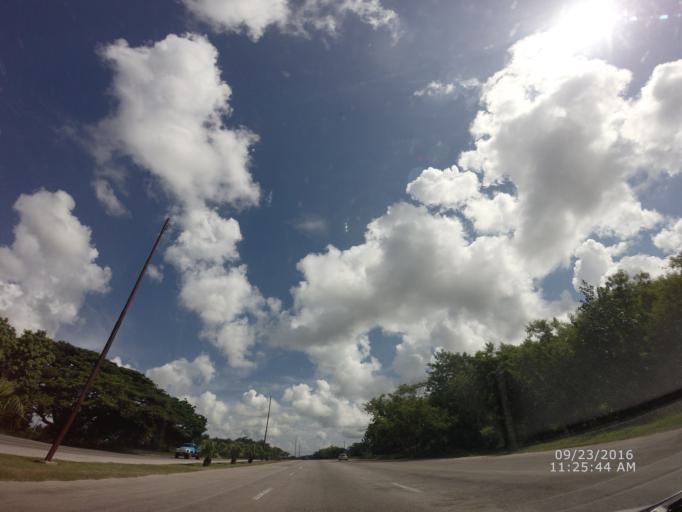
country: CU
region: La Habana
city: San Miguel del Padron
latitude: 23.0667
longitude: -82.2773
